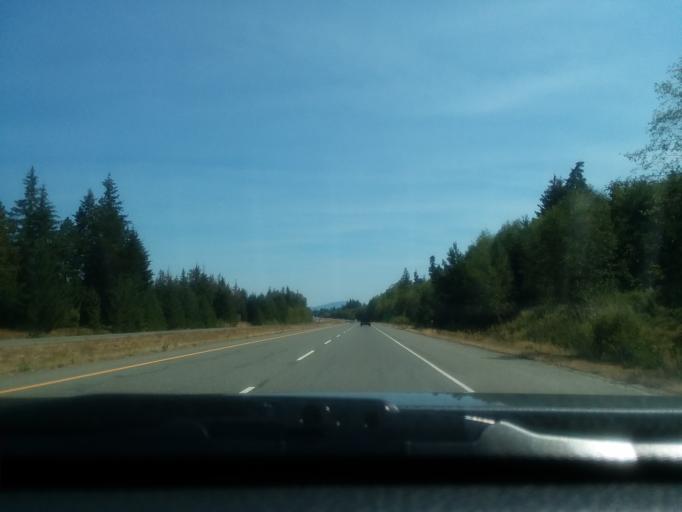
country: CA
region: British Columbia
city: Port Alberni
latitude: 49.3662
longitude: -124.6069
